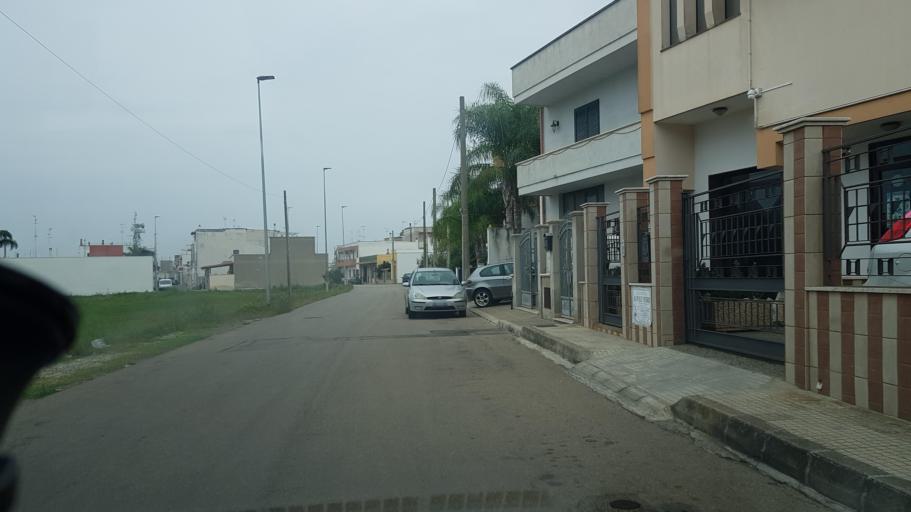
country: IT
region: Apulia
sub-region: Provincia di Lecce
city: Leverano
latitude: 40.2843
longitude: 18.0028
